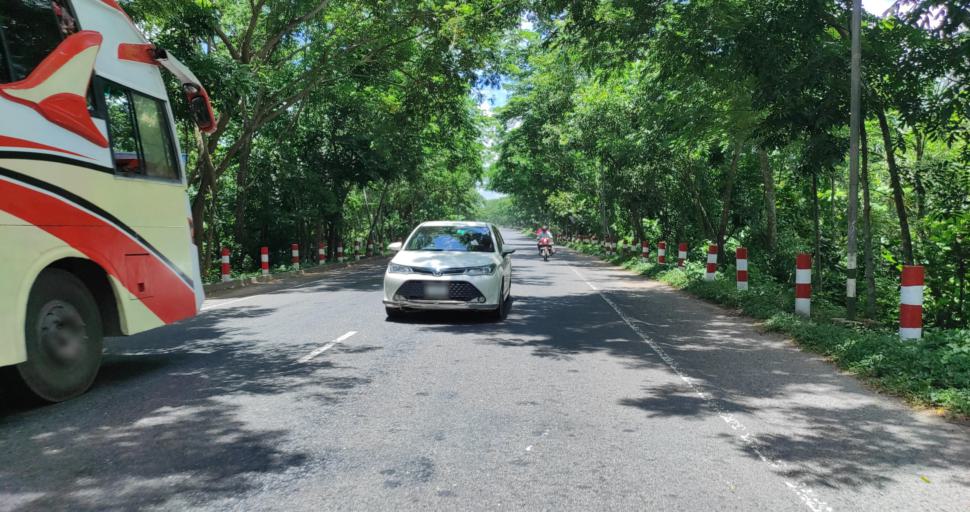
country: BD
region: Barisal
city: Gaurnadi
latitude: 22.8278
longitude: 90.2595
